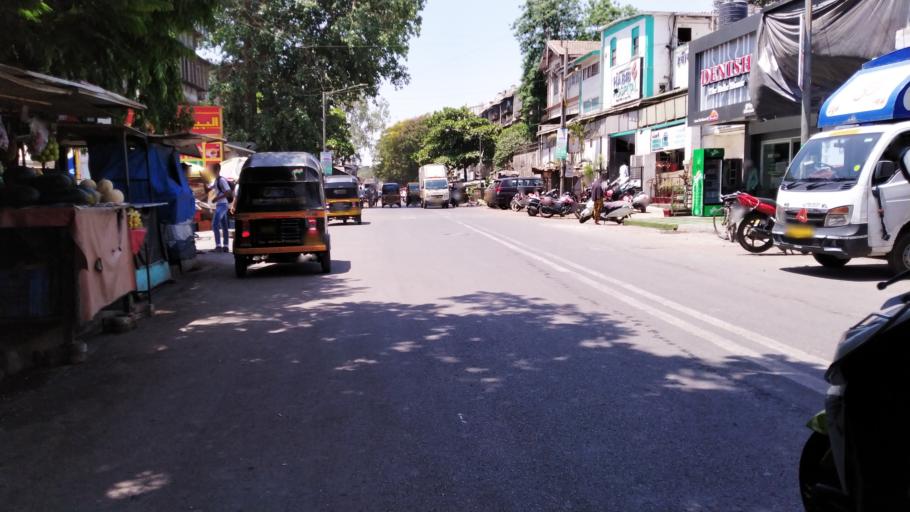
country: IN
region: Maharashtra
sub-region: Mumbai Suburban
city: Mumbai
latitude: 19.0787
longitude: 72.8803
